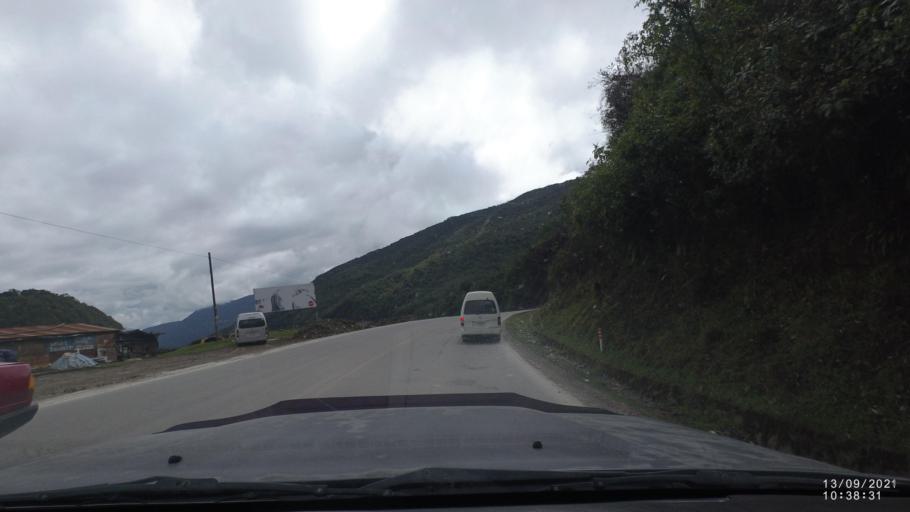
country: BO
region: Cochabamba
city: Colomi
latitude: -17.1963
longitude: -65.8984
